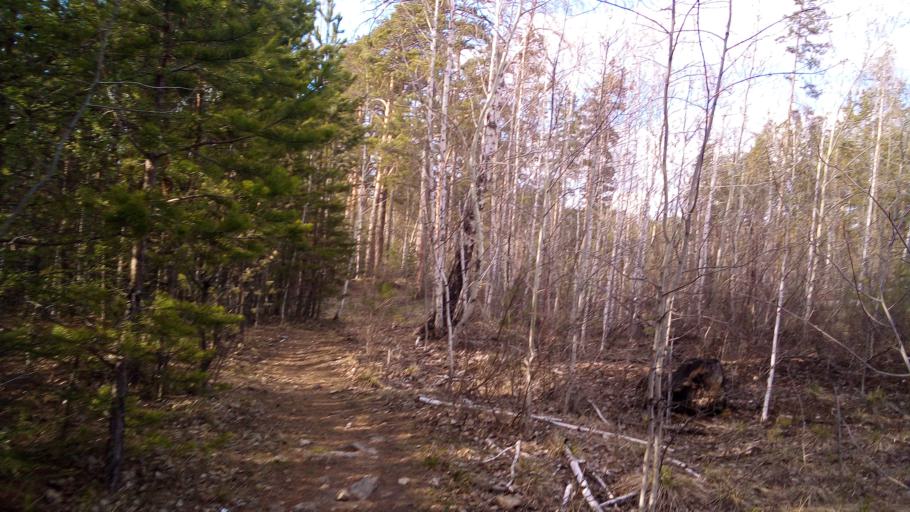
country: RU
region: Chelyabinsk
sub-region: Gorod Chelyabinsk
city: Chelyabinsk
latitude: 55.1639
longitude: 61.3245
